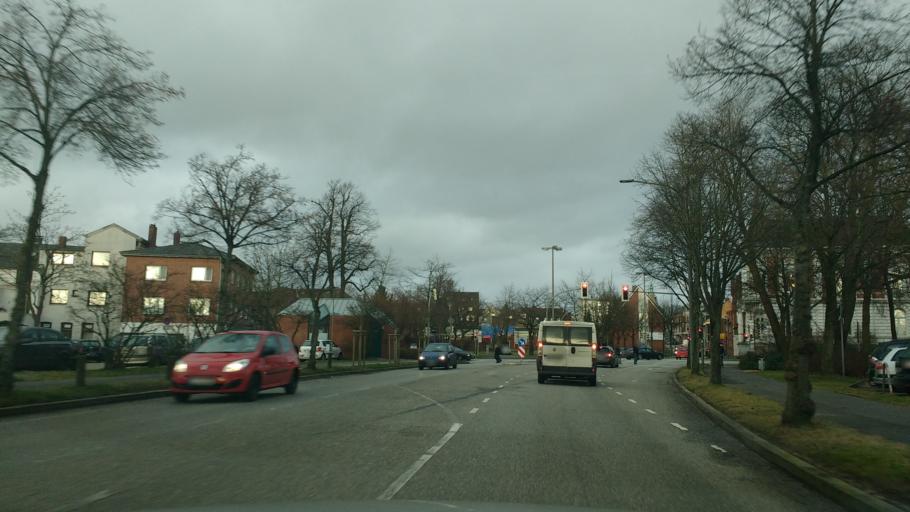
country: DE
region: Schleswig-Holstein
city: Itzehoe
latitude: 53.9200
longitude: 9.5185
